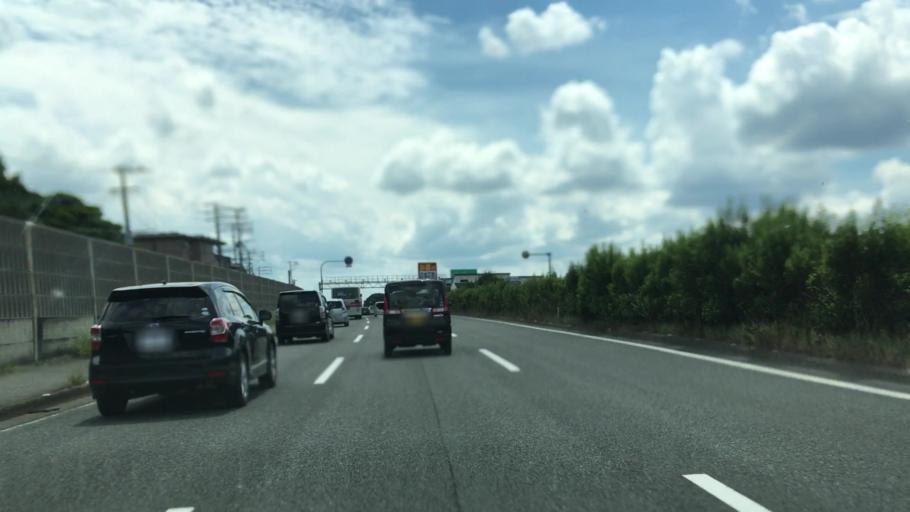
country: JP
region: Fukuoka
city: Chikushino-shi
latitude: 33.4911
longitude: 130.5354
